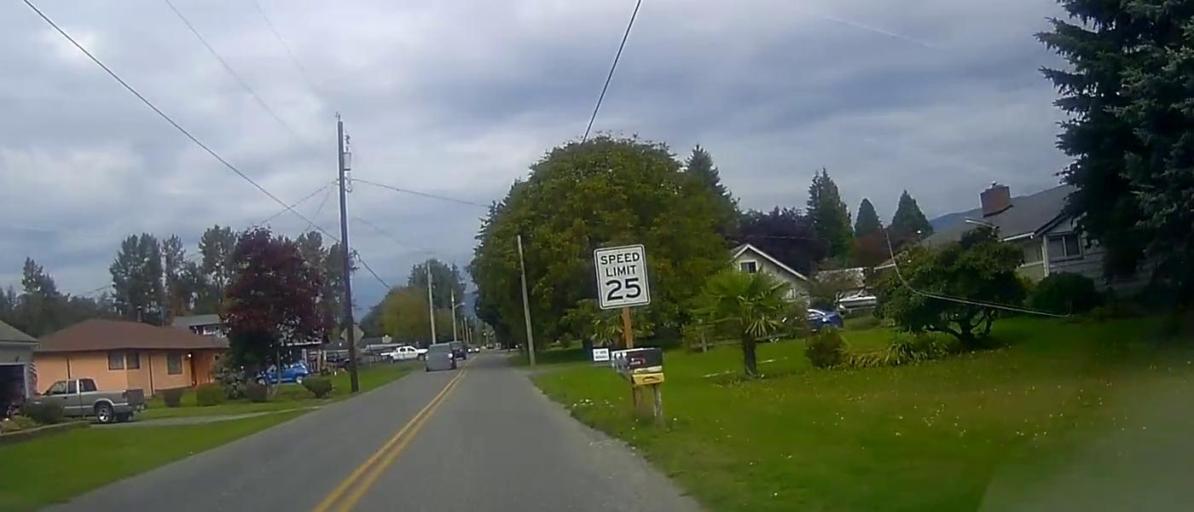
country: US
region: Washington
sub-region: Skagit County
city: Sedro-Woolley
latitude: 48.4975
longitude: -122.2584
